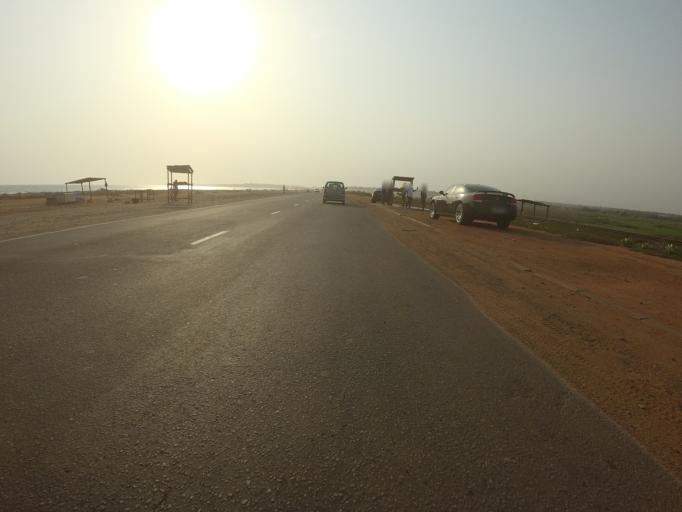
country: GH
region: Greater Accra
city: Nungua
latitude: 5.6136
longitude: -0.0338
